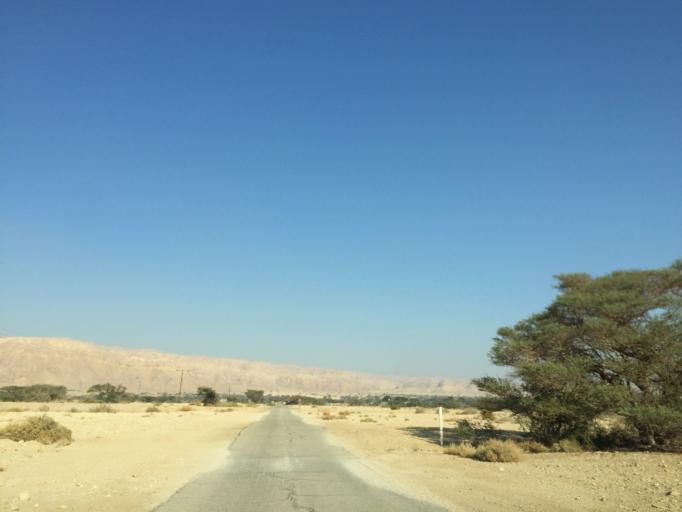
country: JO
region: Ma'an
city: Al Quwayrah
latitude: 29.8408
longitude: 35.0302
